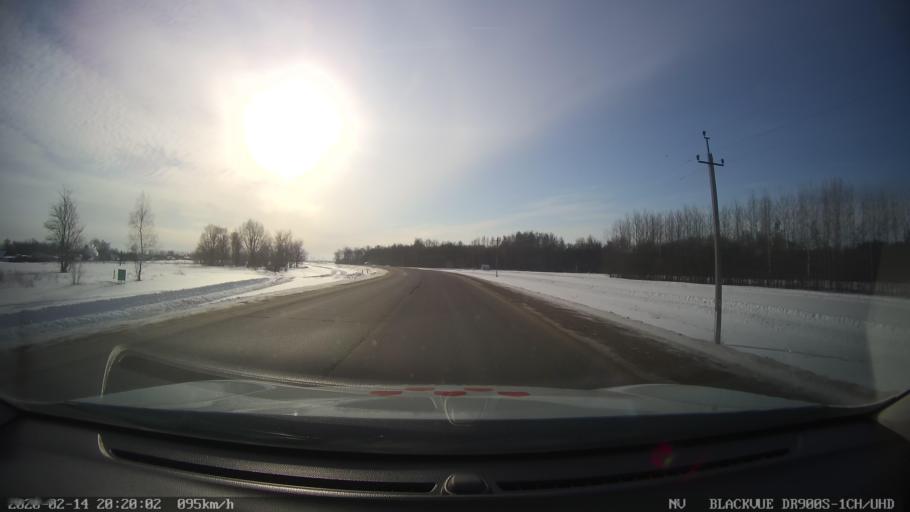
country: RU
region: Tatarstan
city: Verkhniy Uslon
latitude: 55.5618
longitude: 48.9017
